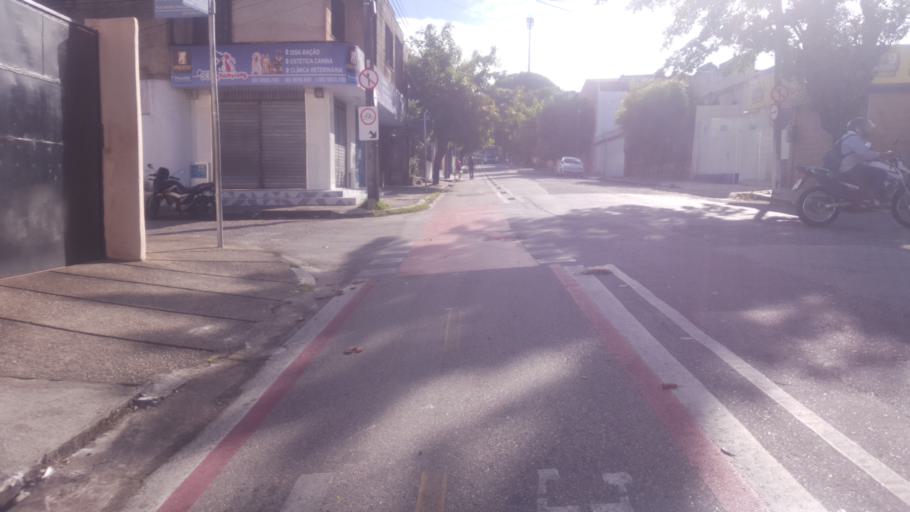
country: BR
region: Ceara
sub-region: Fortaleza
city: Fortaleza
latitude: -3.7453
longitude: -38.5401
